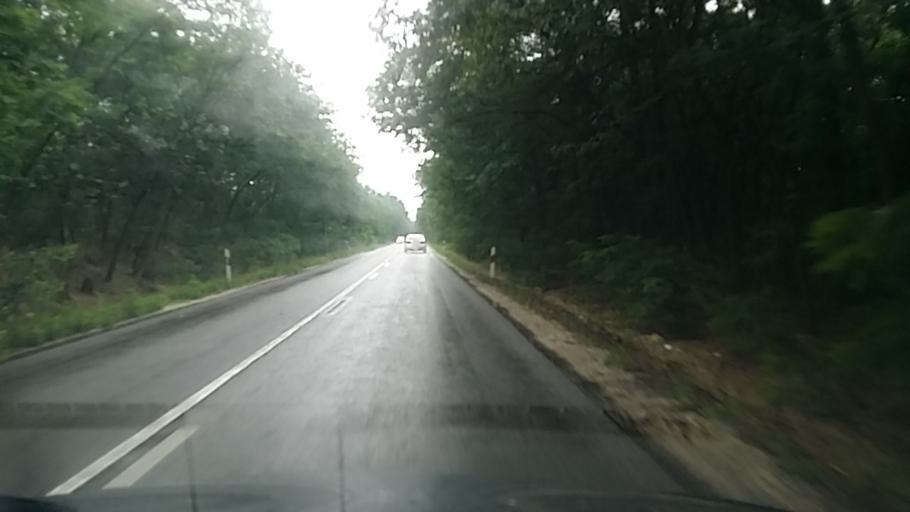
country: HU
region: Pest
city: Ullo
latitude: 47.3417
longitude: 19.3221
